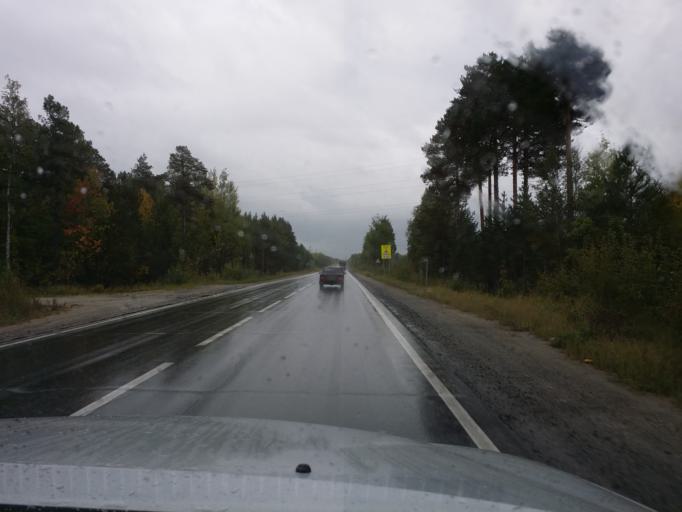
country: RU
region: Khanty-Mansiyskiy Avtonomnyy Okrug
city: Megion
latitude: 61.1535
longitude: 75.7397
